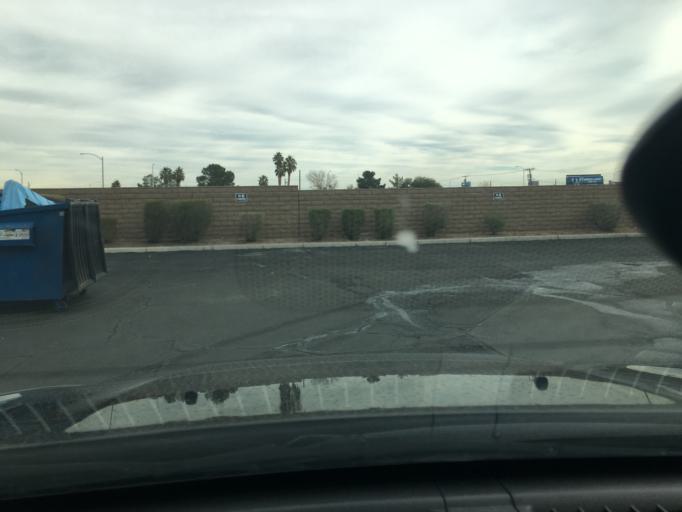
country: US
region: Nevada
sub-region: Clark County
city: Spring Valley
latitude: 36.1608
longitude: -115.2207
